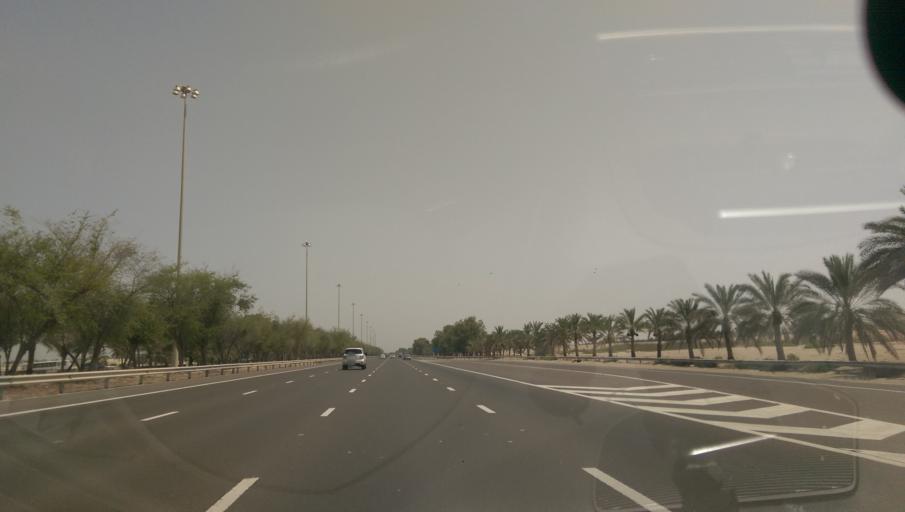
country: AE
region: Abu Dhabi
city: Abu Dhabi
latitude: 24.4413
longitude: 54.6786
